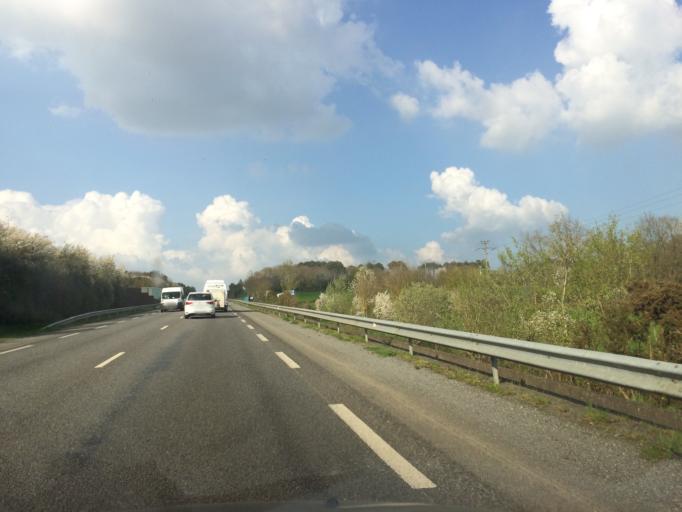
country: FR
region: Pays de la Loire
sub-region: Departement de la Loire-Atlantique
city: Saint-Nicolas-de-Redon
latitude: 47.6382
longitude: -2.0526
